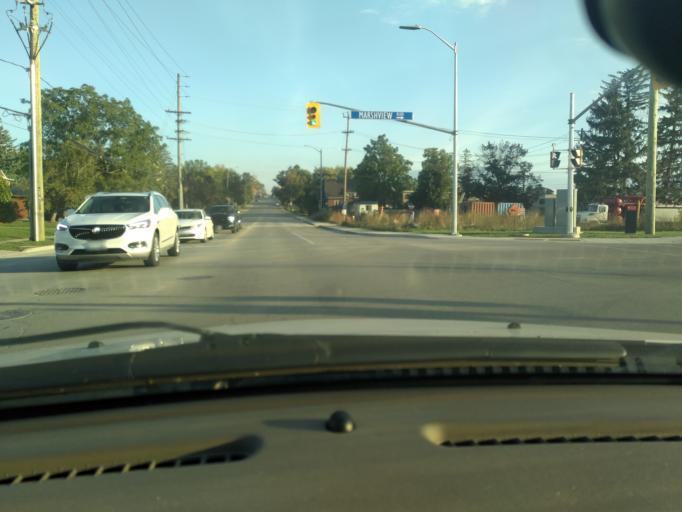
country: CA
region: Ontario
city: Bradford West Gwillimbury
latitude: 44.1098
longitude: -79.5636
